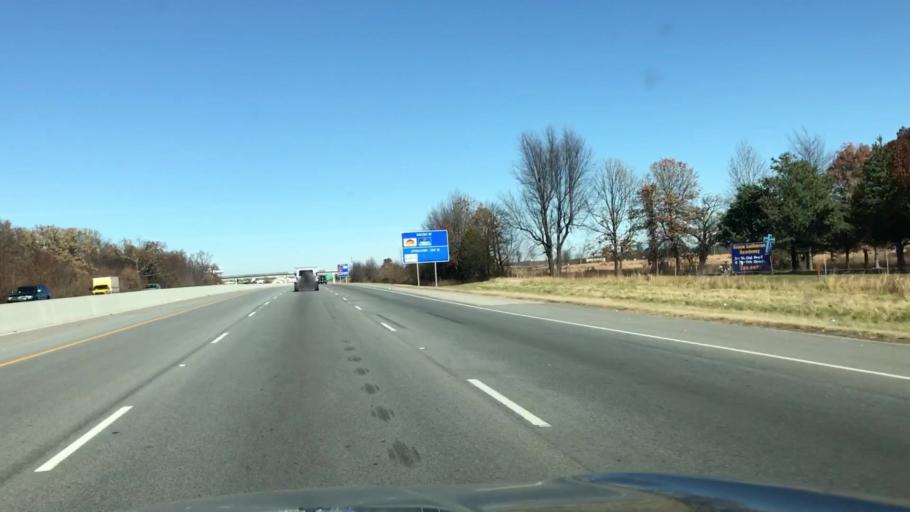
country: US
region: Arkansas
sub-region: Benton County
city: Lowell
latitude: 36.2611
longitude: -94.1502
